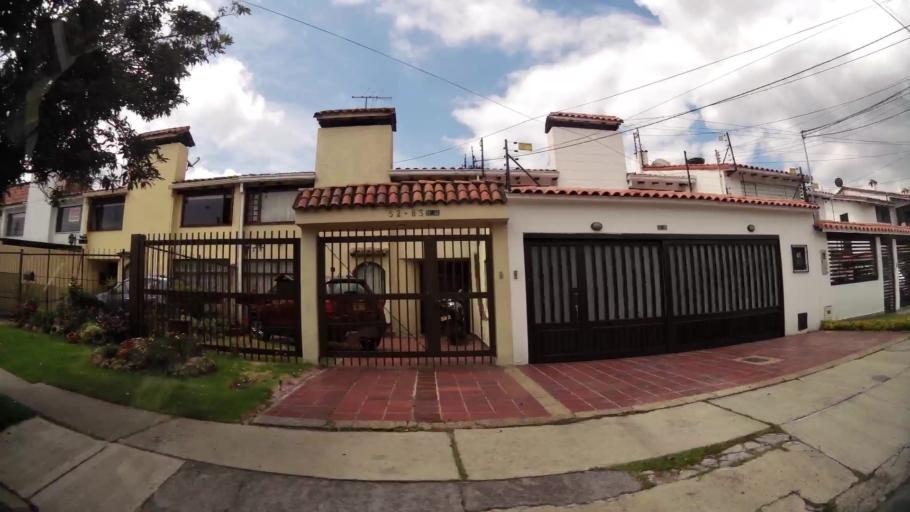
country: CO
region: Bogota D.C.
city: Barrio San Luis
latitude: 4.7028
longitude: -74.0625
